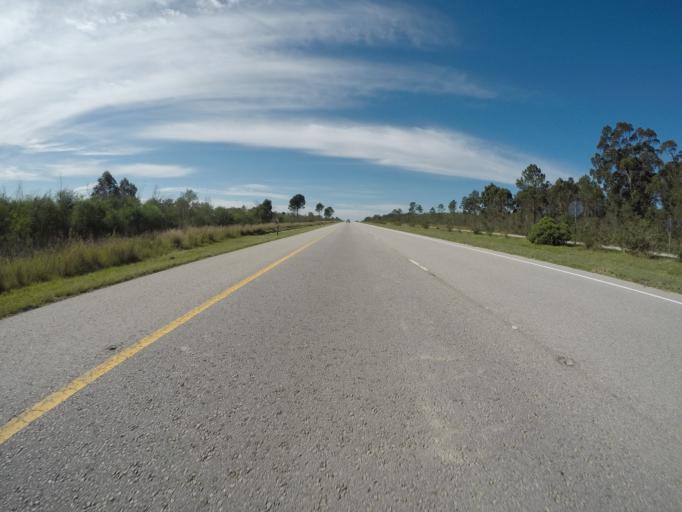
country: ZA
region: Eastern Cape
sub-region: Nelson Mandela Bay Metropolitan Municipality
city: Uitenhage
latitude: -33.9237
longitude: 25.3137
